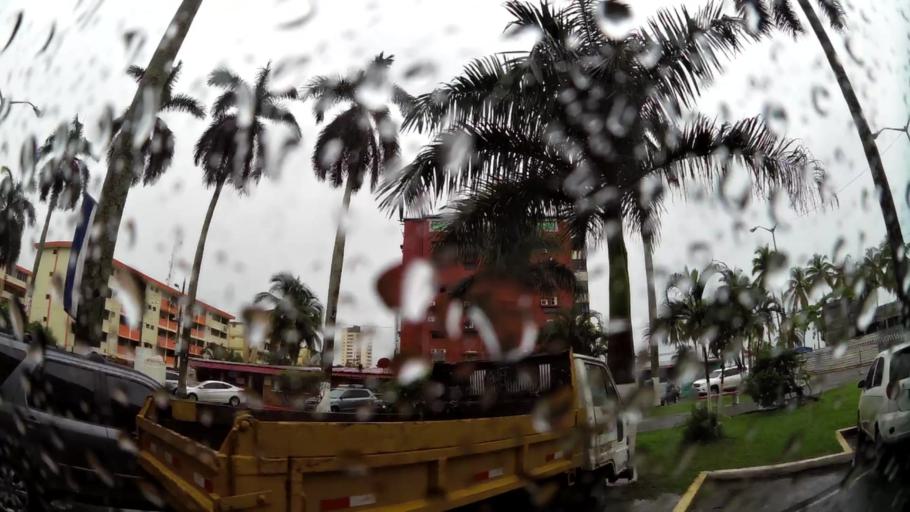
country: PA
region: Colon
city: Colon
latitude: 9.3657
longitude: -79.9039
